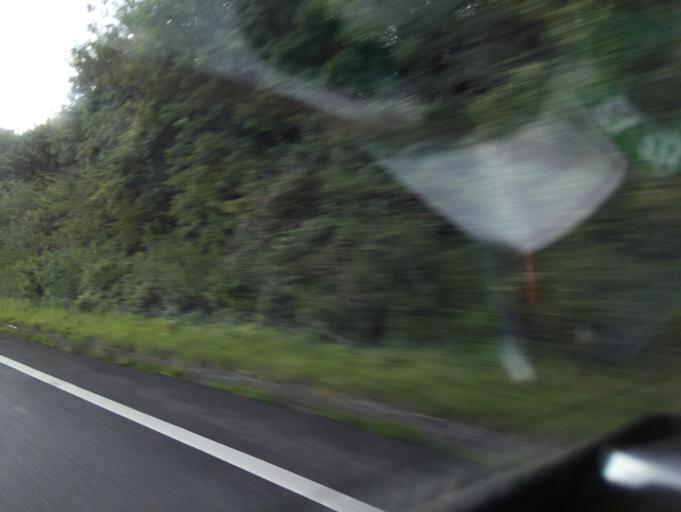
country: GB
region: England
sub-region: Devon
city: Ivybridge
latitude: 50.3845
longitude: -3.9064
